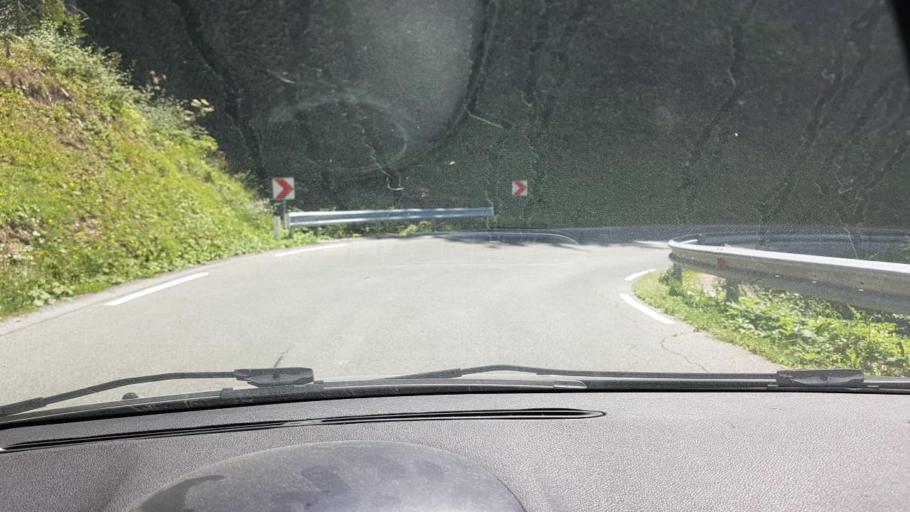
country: SI
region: Jezersko
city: Zgornje Jezersko
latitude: 46.4175
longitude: 14.5268
